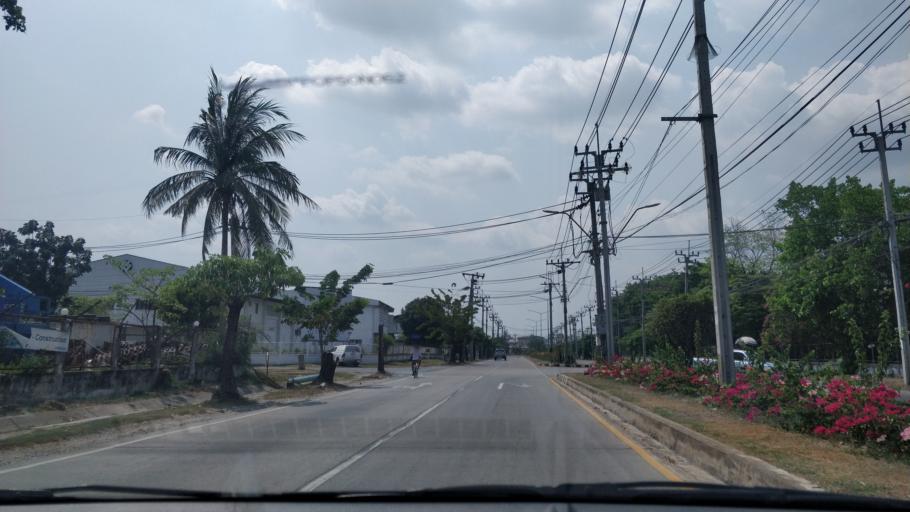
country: TH
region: Bangkok
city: Lat Krabang
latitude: 13.7585
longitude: 100.7869
